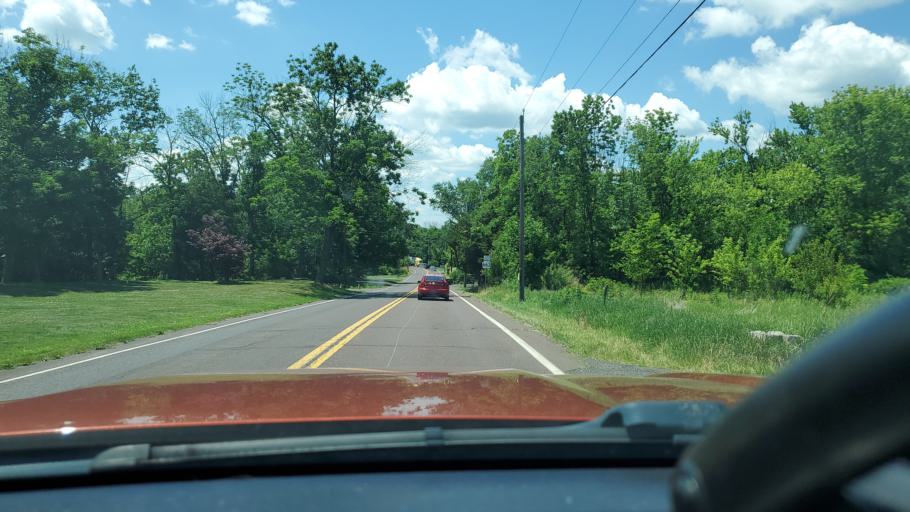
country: US
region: Pennsylvania
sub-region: Montgomery County
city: Gilbertsville
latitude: 40.3191
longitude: -75.5610
